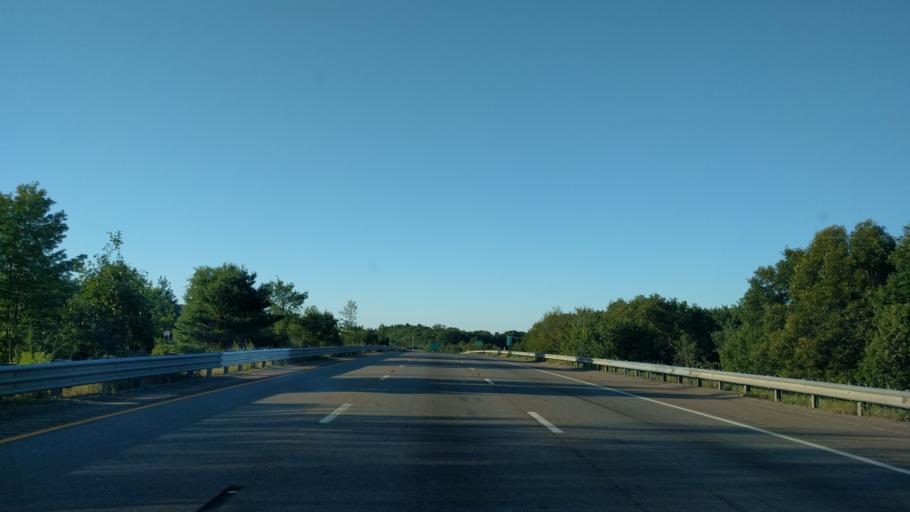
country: US
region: Massachusetts
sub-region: Worcester County
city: Cordaville
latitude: 42.2687
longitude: -71.5650
